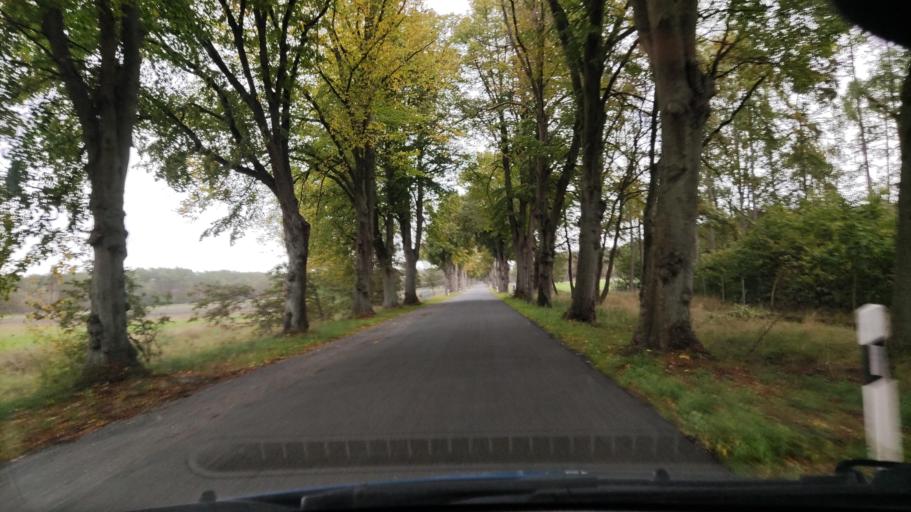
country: DE
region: Saxony-Anhalt
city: Luftkurort Arendsee
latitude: 52.9444
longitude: 11.5337
